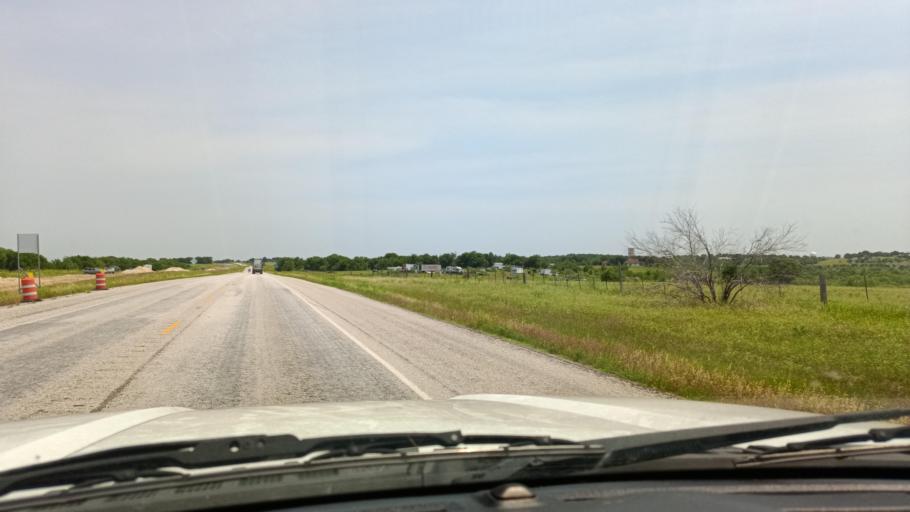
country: US
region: Texas
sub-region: Bell County
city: Rogers
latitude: 30.9647
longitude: -97.2636
